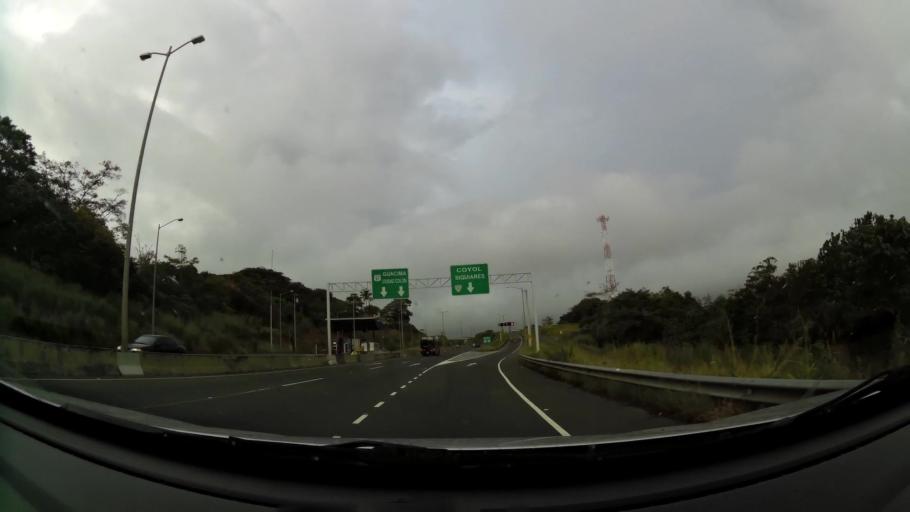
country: CR
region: Alajuela
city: Carrillos
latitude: 9.9648
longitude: -84.2838
